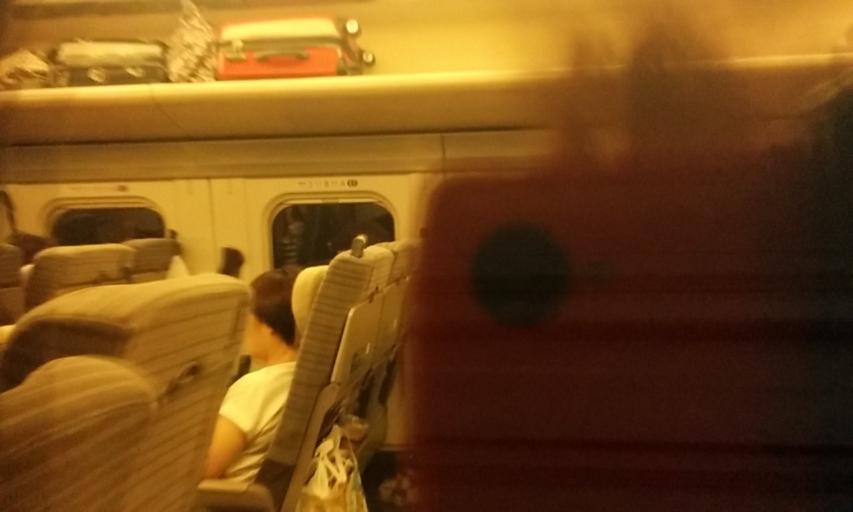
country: JP
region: Miyagi
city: Okawara
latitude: 38.0360
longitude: 140.6806
